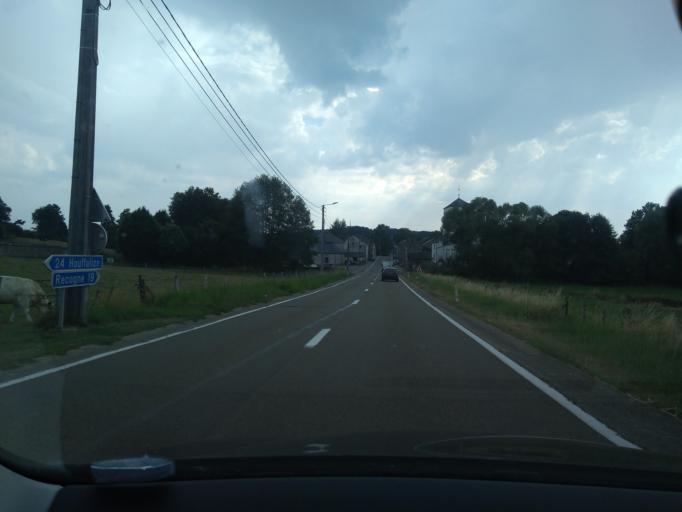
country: BE
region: Wallonia
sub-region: Province du Luxembourg
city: Sainte-Ode
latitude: 50.0297
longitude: 5.5268
